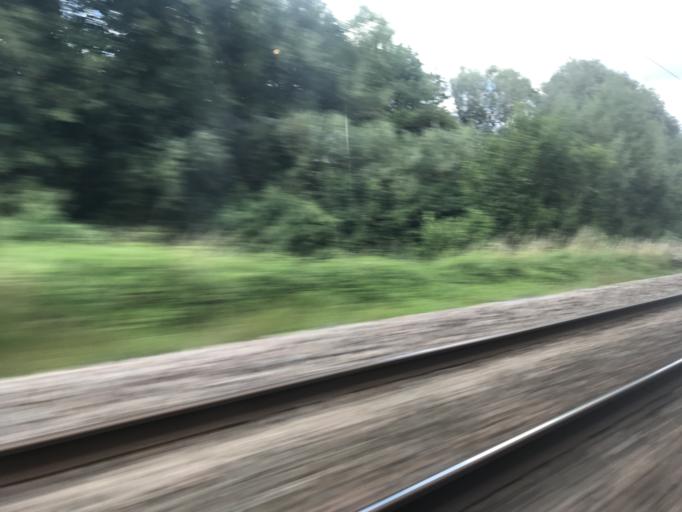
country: FR
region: Champagne-Ardenne
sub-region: Departement des Ardennes
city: Bazeilles
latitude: 49.6672
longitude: 4.9655
